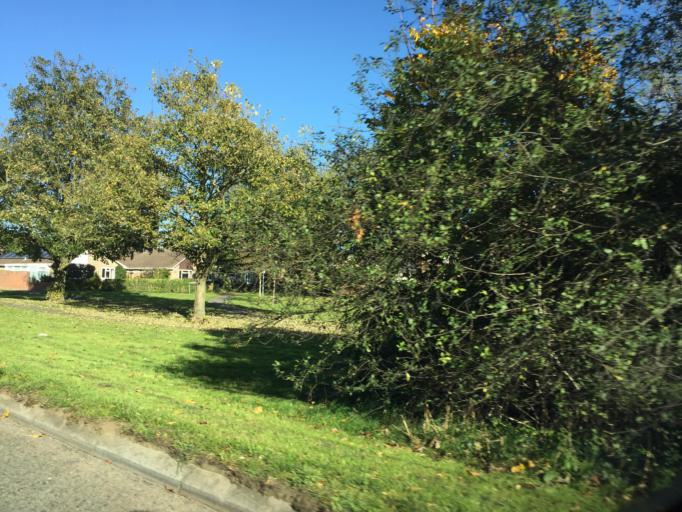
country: GB
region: England
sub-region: South Gloucestershire
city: Yate
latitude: 51.5439
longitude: -2.4093
